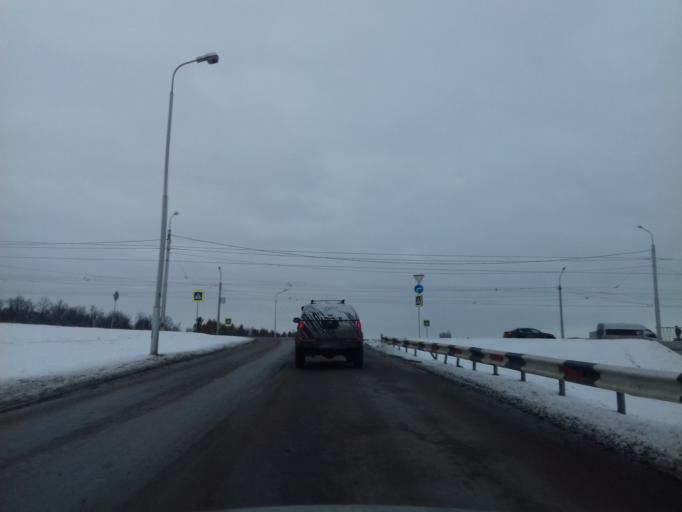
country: RU
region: Bashkortostan
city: Ufa
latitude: 54.7508
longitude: 56.0186
